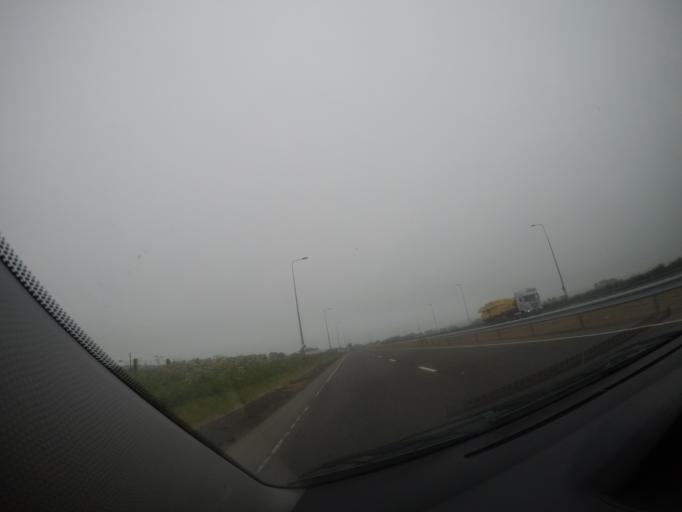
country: GB
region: Scotland
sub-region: Angus
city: Forfar
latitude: 56.5708
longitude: -2.9173
